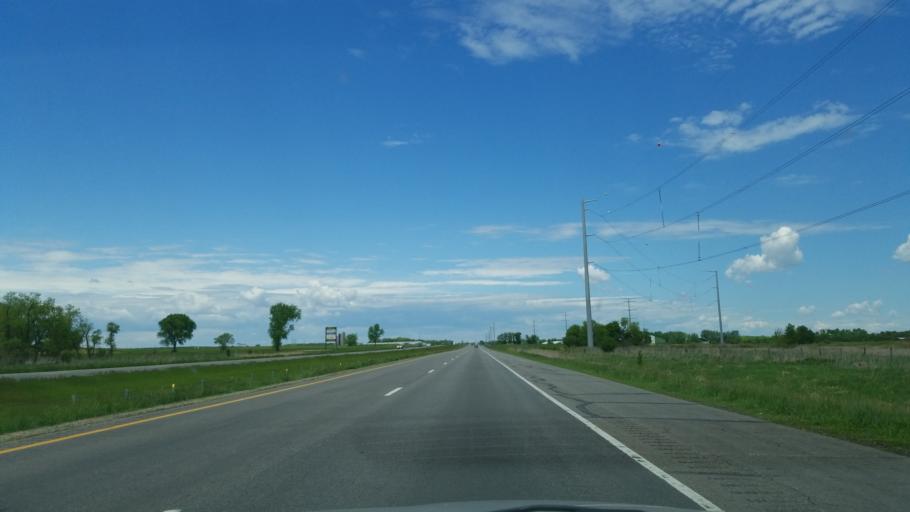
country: US
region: Minnesota
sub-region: Stearns County
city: Melrose
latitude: 45.6761
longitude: -94.8359
